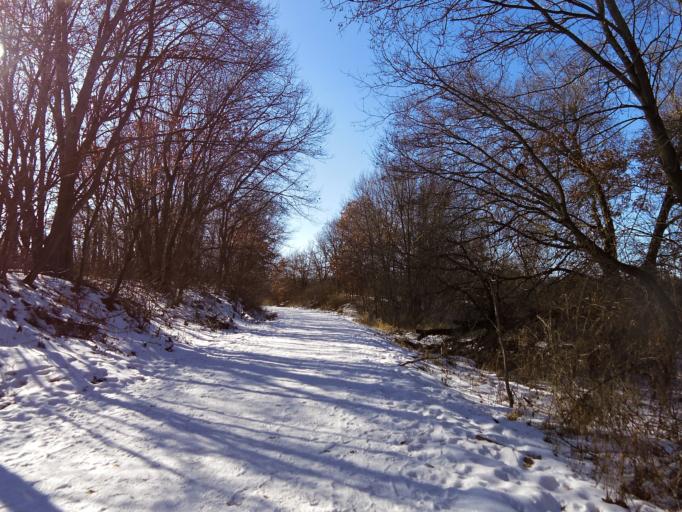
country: US
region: Minnesota
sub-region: Washington County
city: Stillwater
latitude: 45.0756
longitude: -92.8318
